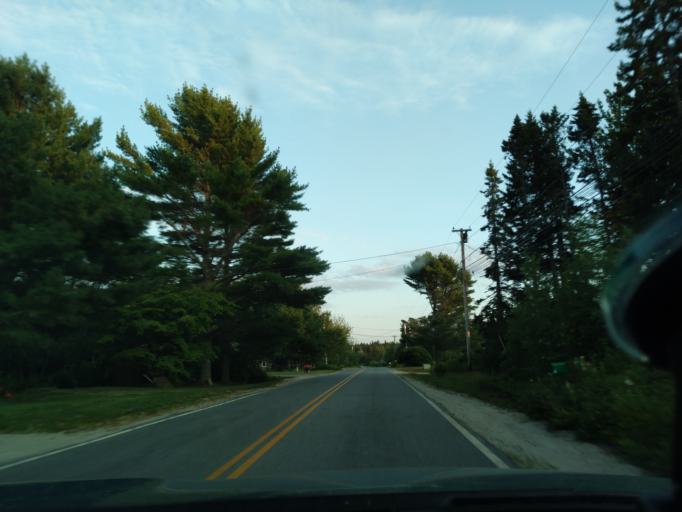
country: US
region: Maine
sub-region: Hancock County
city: Gouldsboro
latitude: 44.3756
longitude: -68.0354
